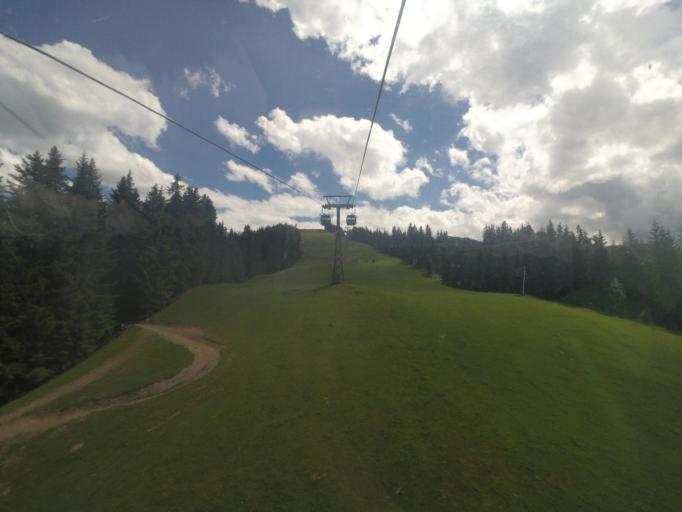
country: AT
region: Salzburg
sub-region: Politischer Bezirk Zell am See
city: Leogang
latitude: 47.4199
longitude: 12.7141
